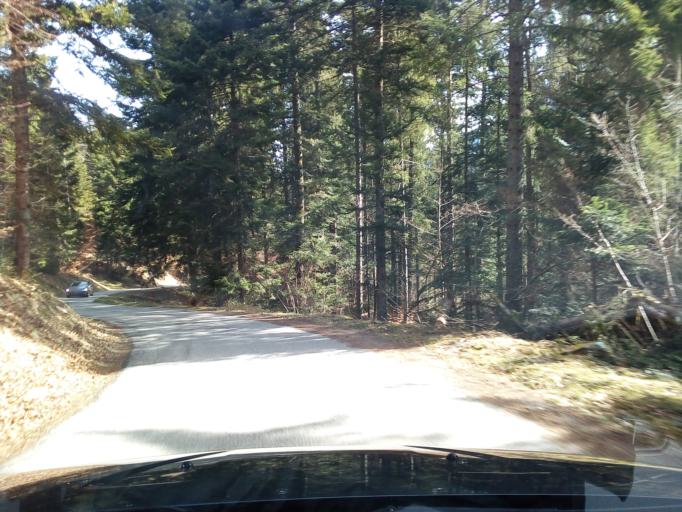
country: FR
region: Rhone-Alpes
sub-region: Departement de l'Isere
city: Revel
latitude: 45.1589
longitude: 5.8744
